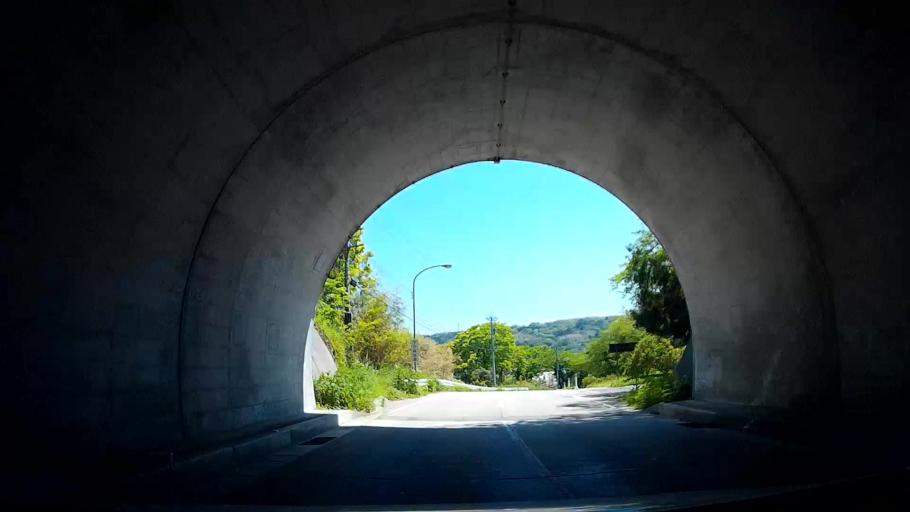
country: JP
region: Ishikawa
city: Nanao
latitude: 37.5301
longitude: 137.2748
